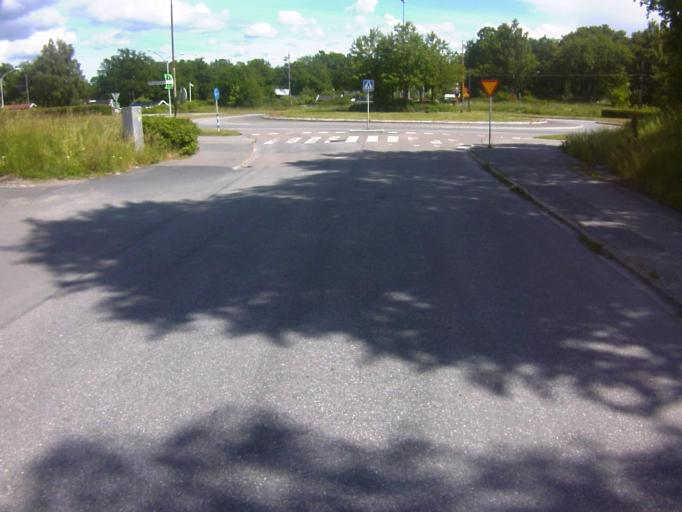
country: SE
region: Soedermanland
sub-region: Eskilstuna Kommun
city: Skogstorp
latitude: 59.3463
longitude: 16.4917
